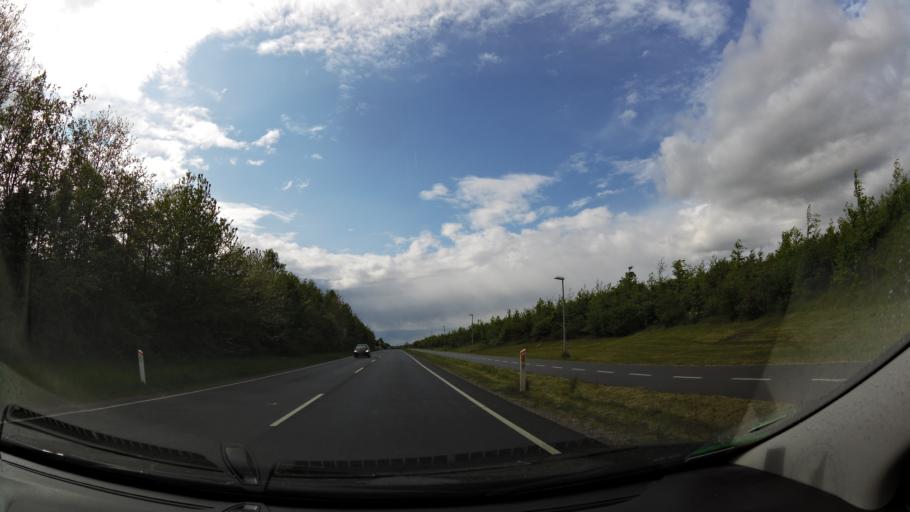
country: DK
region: South Denmark
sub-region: Nyborg Kommune
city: Nyborg
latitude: 55.3137
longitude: 10.7624
